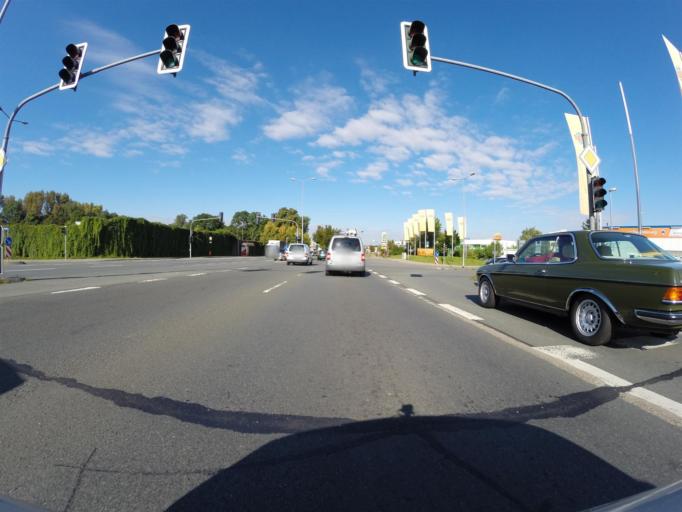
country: DE
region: Thuringia
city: Monchenholzhausen
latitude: 50.9751
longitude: 11.1079
